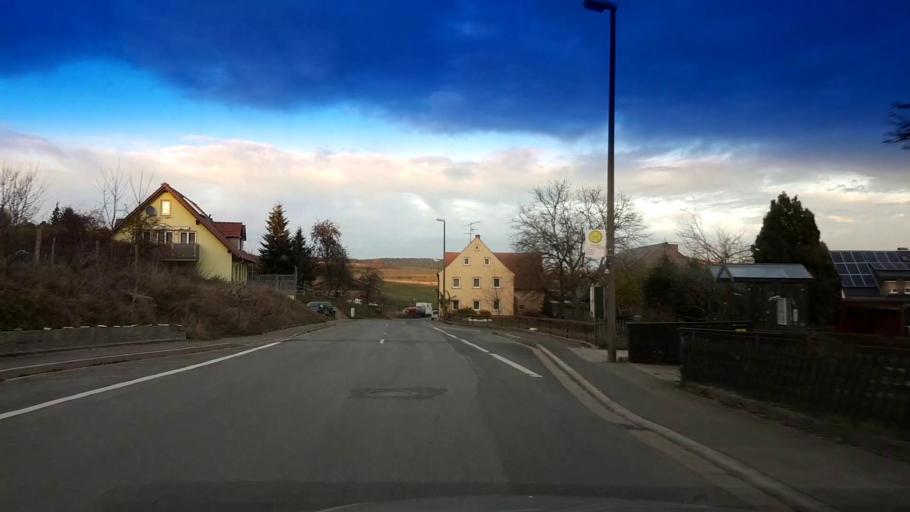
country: DE
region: Bavaria
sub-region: Upper Franconia
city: Priesendorf
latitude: 49.8861
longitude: 10.7278
